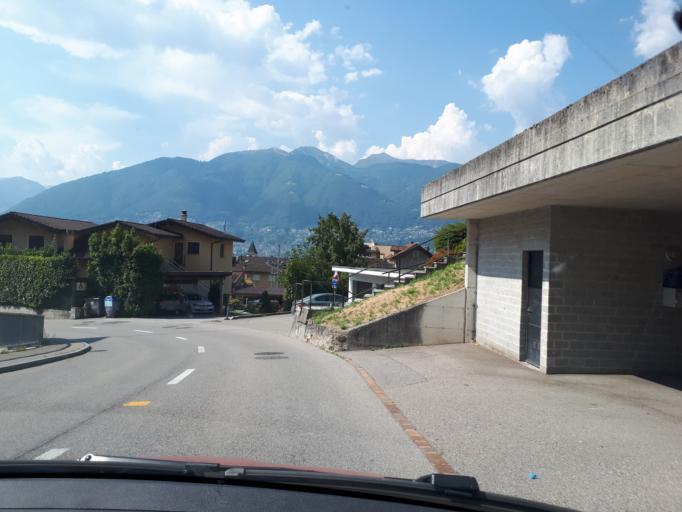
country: CH
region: Ticino
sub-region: Locarno District
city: Magadino
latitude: 46.1428
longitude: 8.8431
